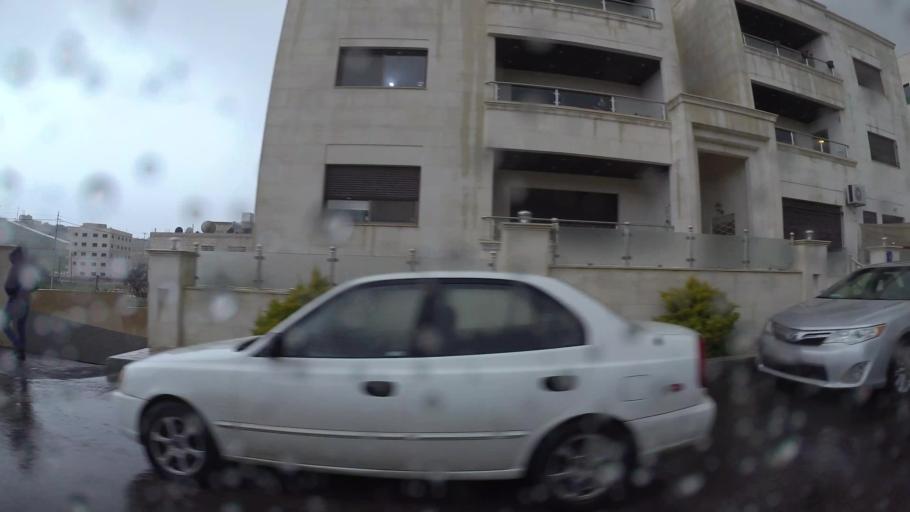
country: JO
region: Amman
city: Umm as Summaq
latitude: 31.8789
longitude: 35.8569
